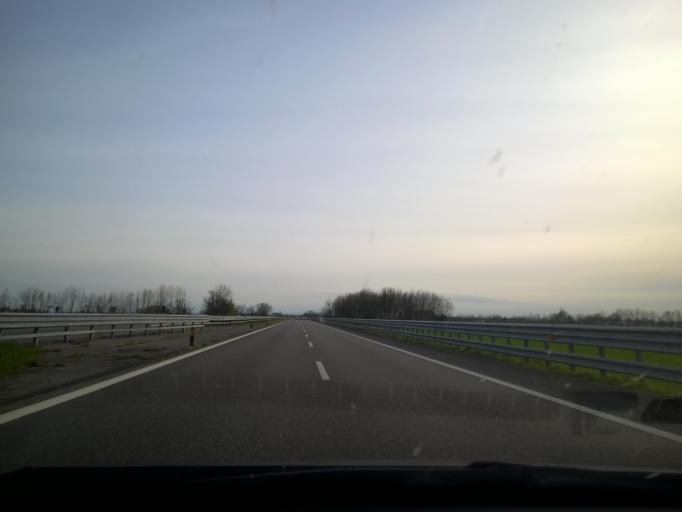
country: IT
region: Lombardy
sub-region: Provincia di Cremona
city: Persico Dosimo
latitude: 45.1952
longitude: 10.0980
